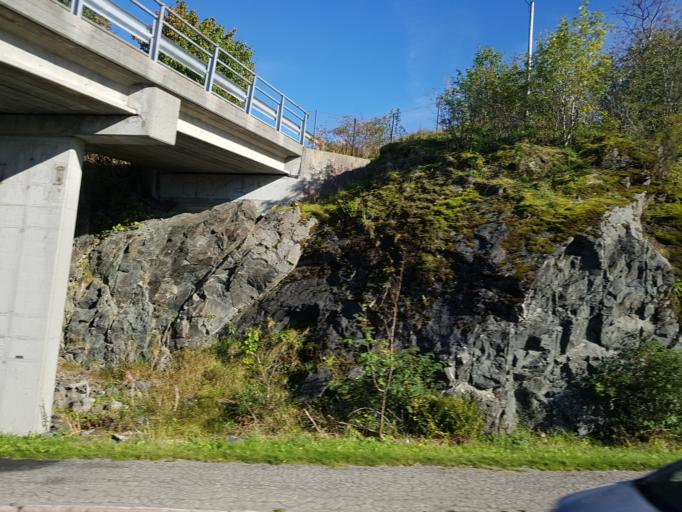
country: NO
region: Sor-Trondelag
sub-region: Skaun
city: Borsa
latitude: 63.4473
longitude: 10.1922
